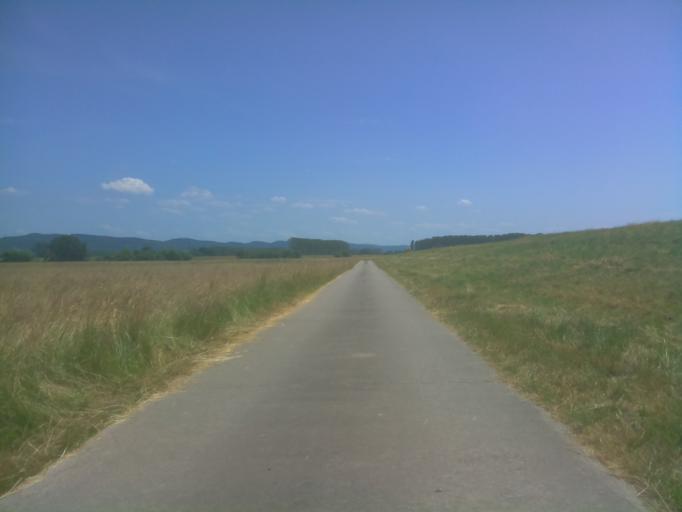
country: DE
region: Hesse
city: Lorsch
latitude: 49.6311
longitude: 8.5903
